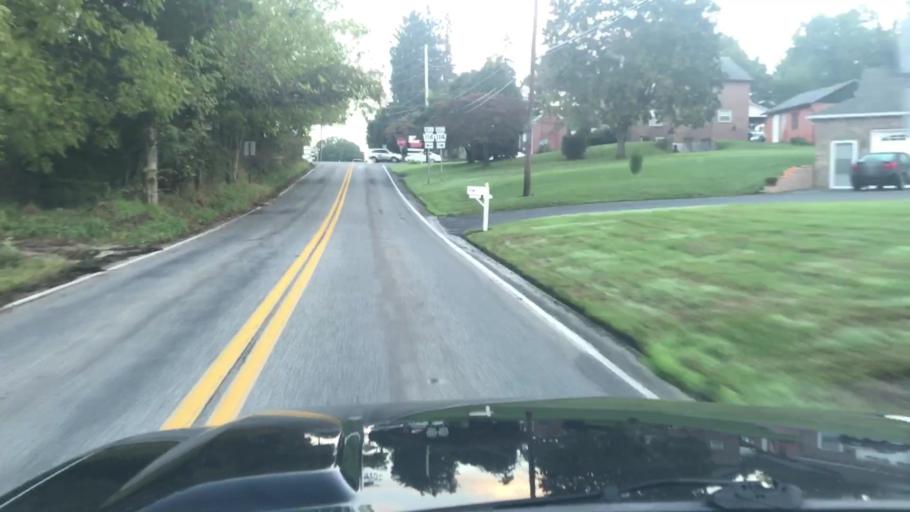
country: US
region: Pennsylvania
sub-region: Cumberland County
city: Lower Allen
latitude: 40.1676
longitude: -76.9212
